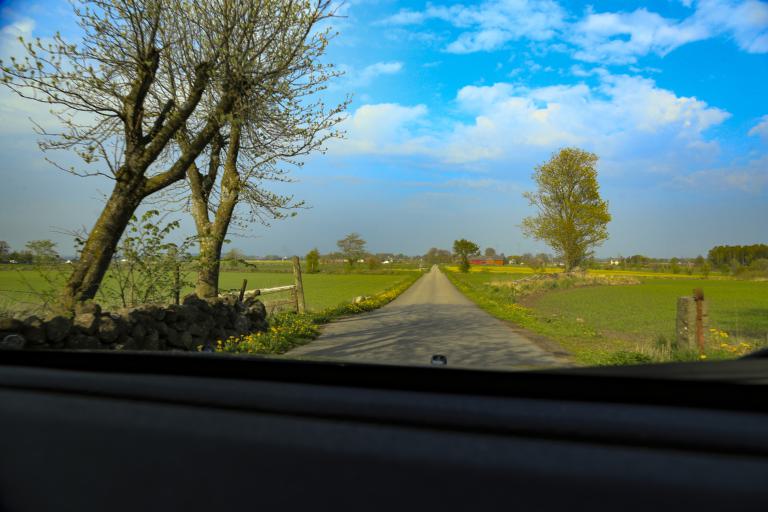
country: SE
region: Halland
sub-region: Varbergs Kommun
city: Traslovslage
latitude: 57.0899
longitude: 12.3250
